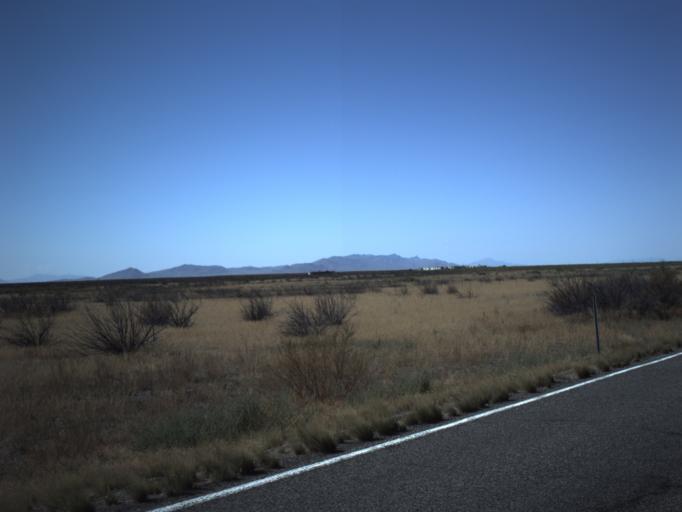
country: US
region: Utah
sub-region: Millard County
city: Delta
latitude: 39.2898
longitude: -112.8295
